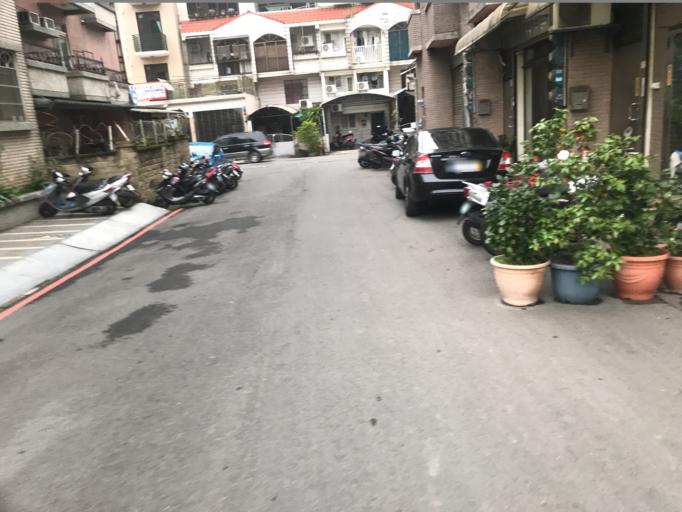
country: TW
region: Taiwan
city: Taoyuan City
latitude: 24.9536
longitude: 121.2372
